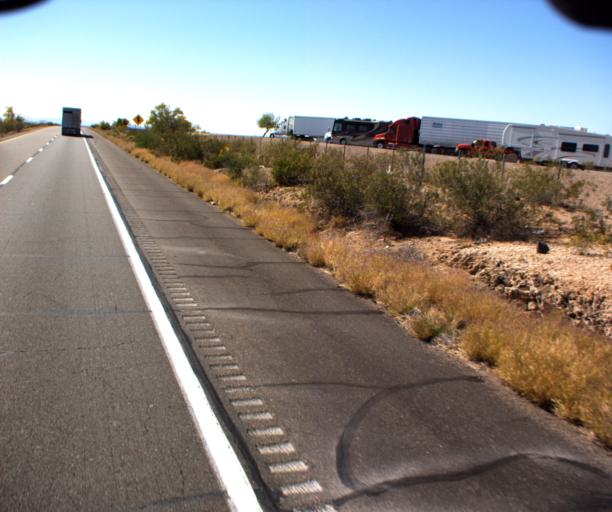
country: US
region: Arizona
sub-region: Maricopa County
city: Gila Bend
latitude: 32.8545
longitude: -113.2523
